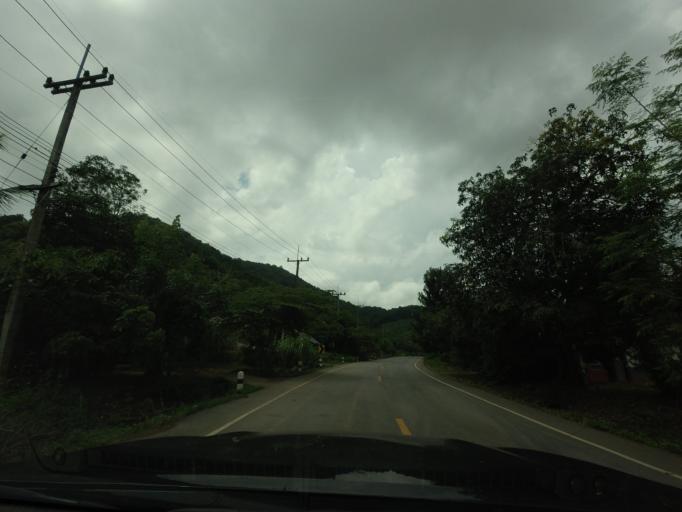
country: TH
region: Loei
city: Pak Chom
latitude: 18.0620
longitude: 101.7951
